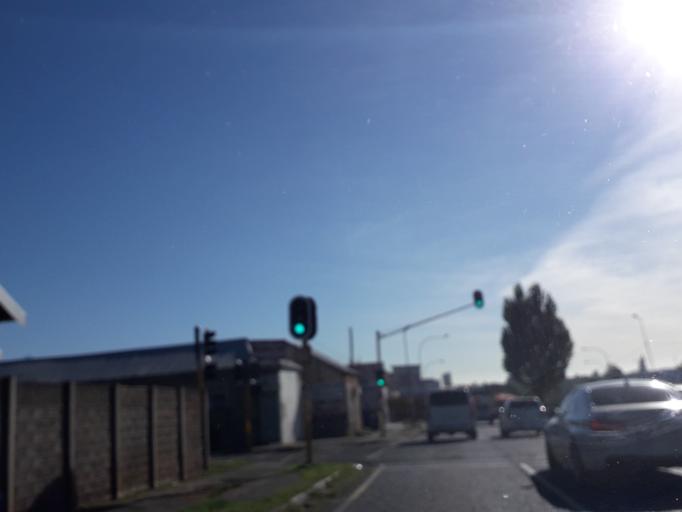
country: ZA
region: Gauteng
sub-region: City of Johannesburg Metropolitan Municipality
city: Roodepoort
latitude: -26.1738
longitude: 27.9588
